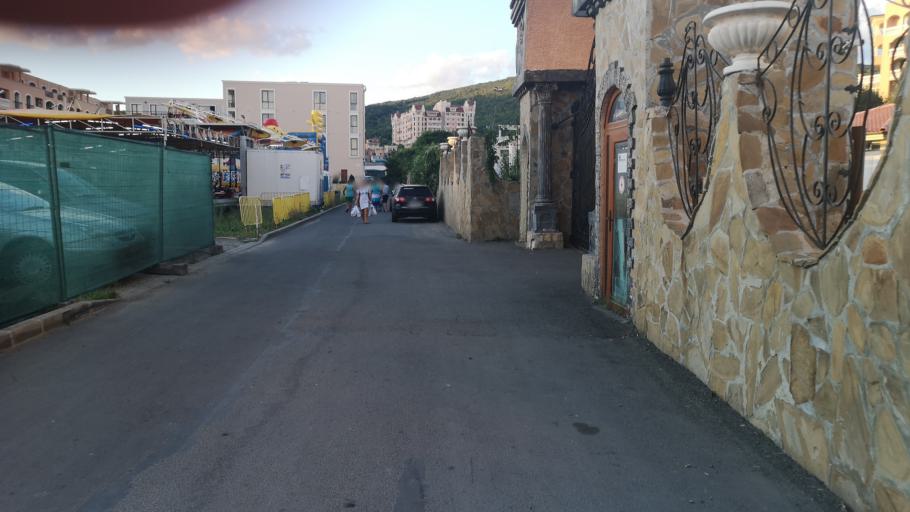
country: BG
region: Burgas
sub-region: Obshtina Nesebur
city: Sveti Vlas
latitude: 42.7024
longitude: 27.8097
